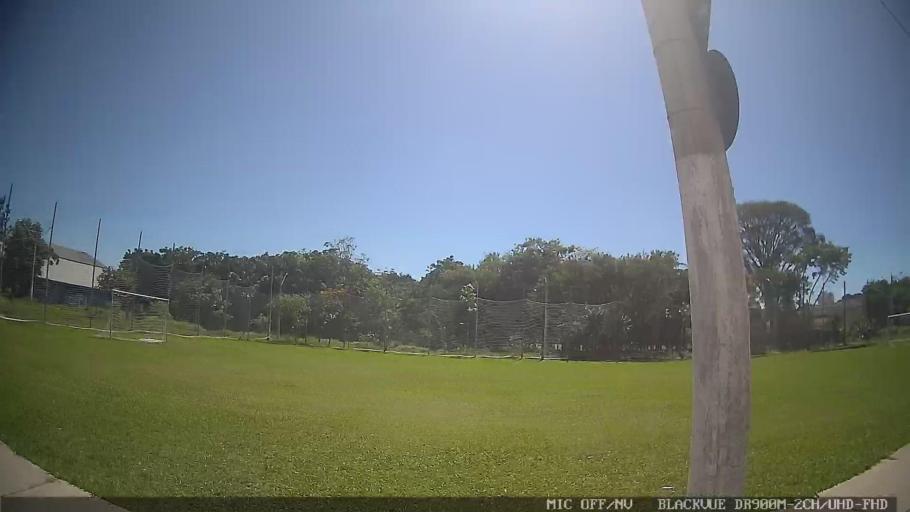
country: BR
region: Sao Paulo
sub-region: Atibaia
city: Atibaia
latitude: -23.1110
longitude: -46.5651
